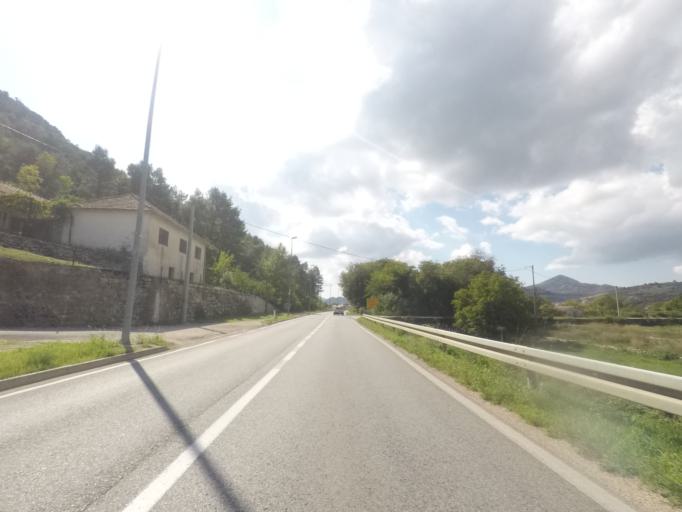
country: BA
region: Republika Srpska
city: Trebinje
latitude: 42.6931
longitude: 18.3392
